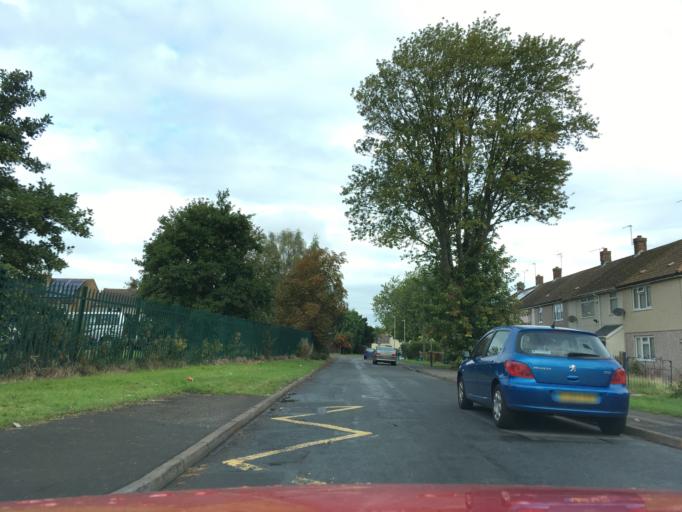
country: GB
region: England
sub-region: Gloucestershire
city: Uckington
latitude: 51.9075
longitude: -2.1166
